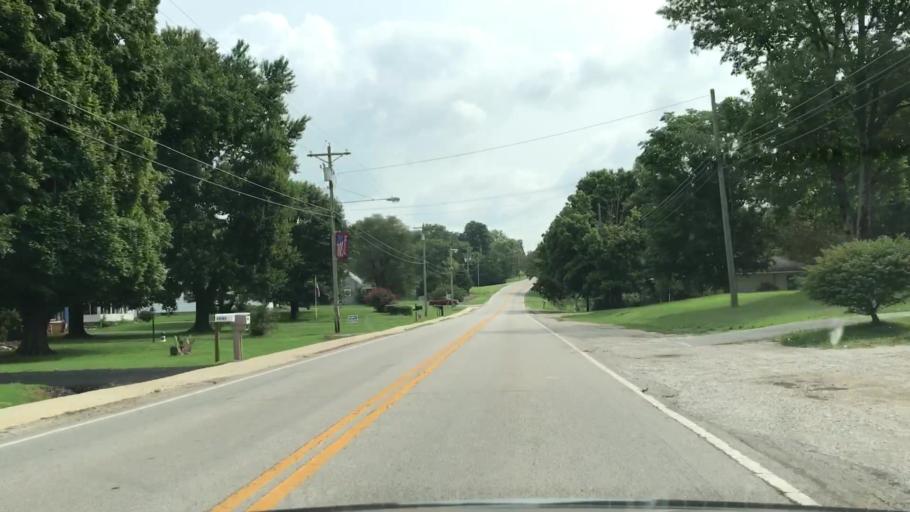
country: US
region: Kentucky
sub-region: Barren County
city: Cave City
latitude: 37.0954
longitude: -86.0411
